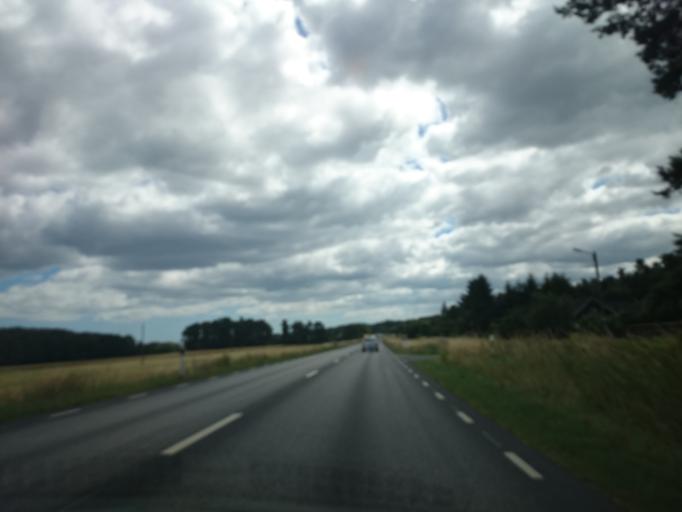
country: SE
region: Skane
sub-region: Kristianstads Kommun
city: Degeberga
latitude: 55.8123
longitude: 14.1368
